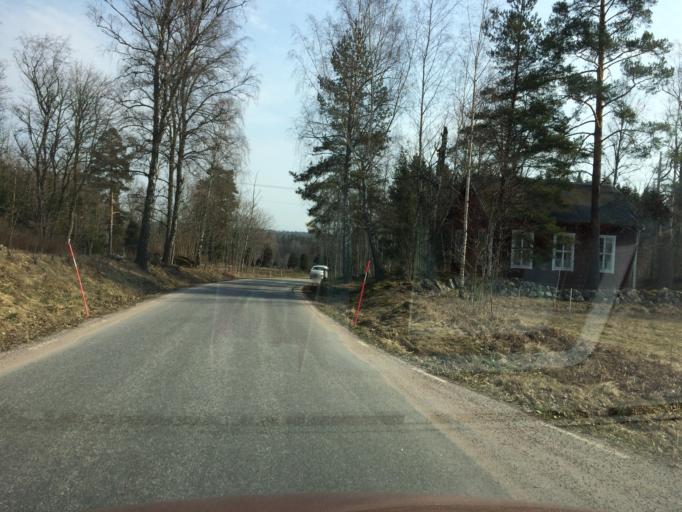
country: SE
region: Soedermanland
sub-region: Vingakers Kommun
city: Vingaker
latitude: 59.0944
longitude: 16.0344
